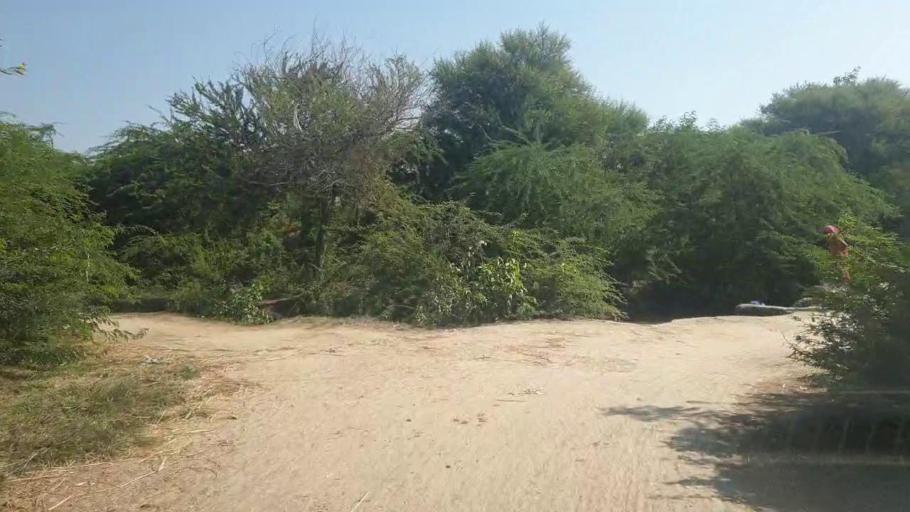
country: PK
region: Sindh
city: Badin
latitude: 24.6835
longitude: 68.8780
